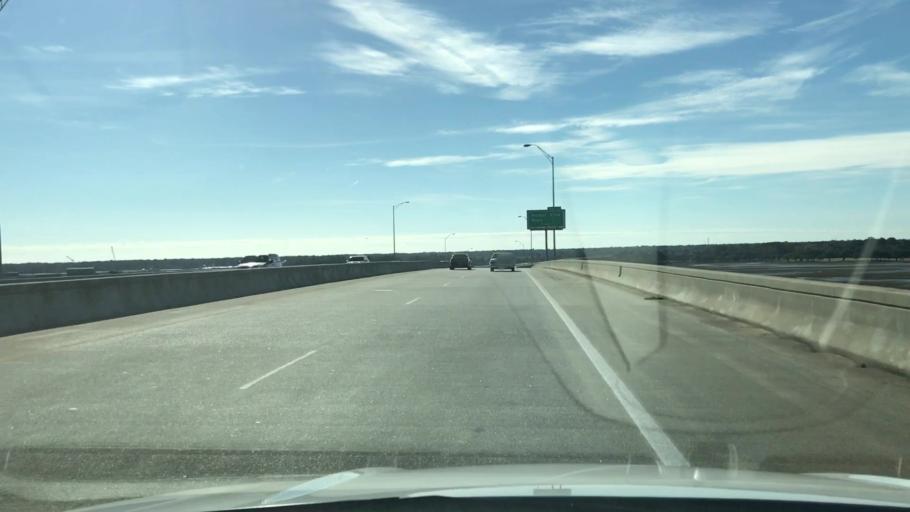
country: US
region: South Carolina
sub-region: Charleston County
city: Charleston
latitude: 32.7702
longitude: -79.9582
